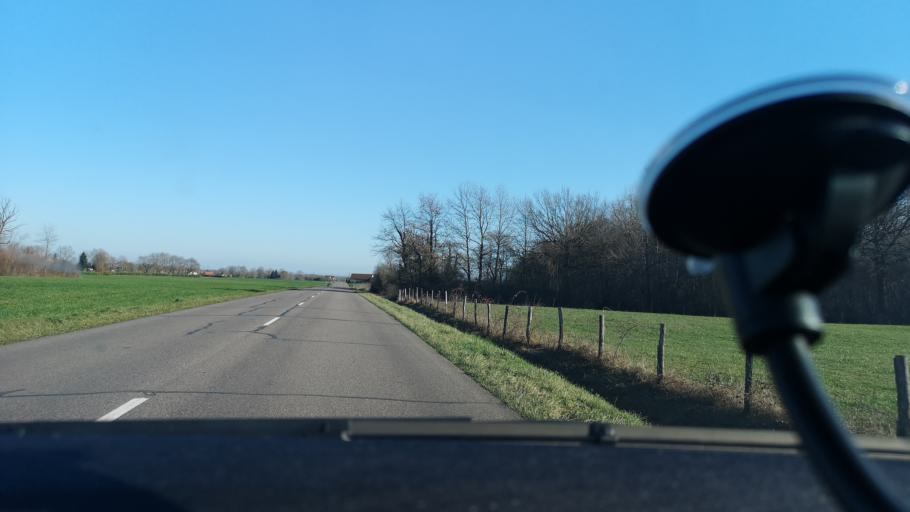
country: FR
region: Bourgogne
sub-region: Departement de Saone-et-Loire
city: Mervans
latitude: 46.7459
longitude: 5.1466
